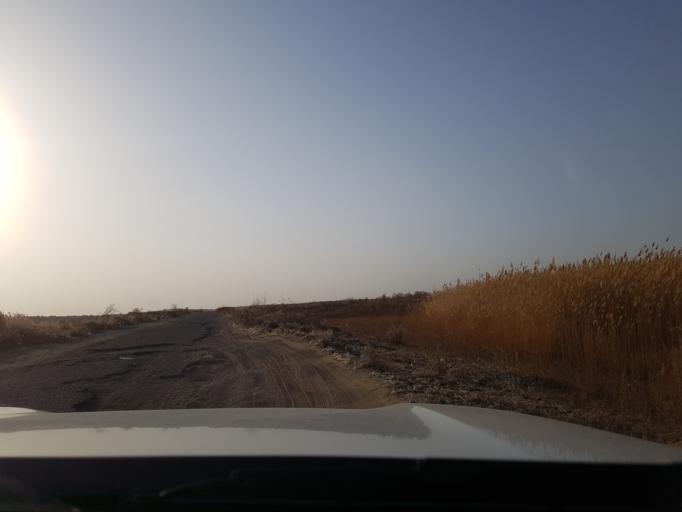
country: UZ
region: Xorazm
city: Hazorasp
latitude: 41.1687
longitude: 60.7917
